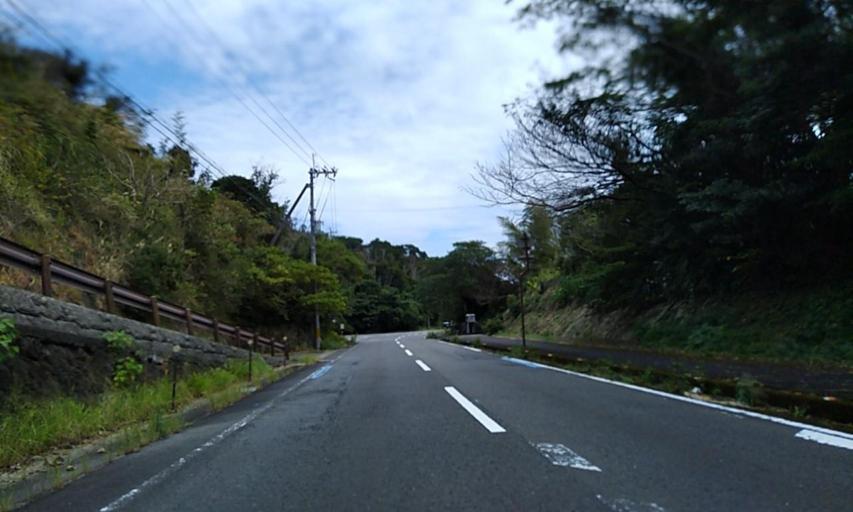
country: JP
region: Wakayama
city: Shingu
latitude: 33.4711
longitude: 135.8096
